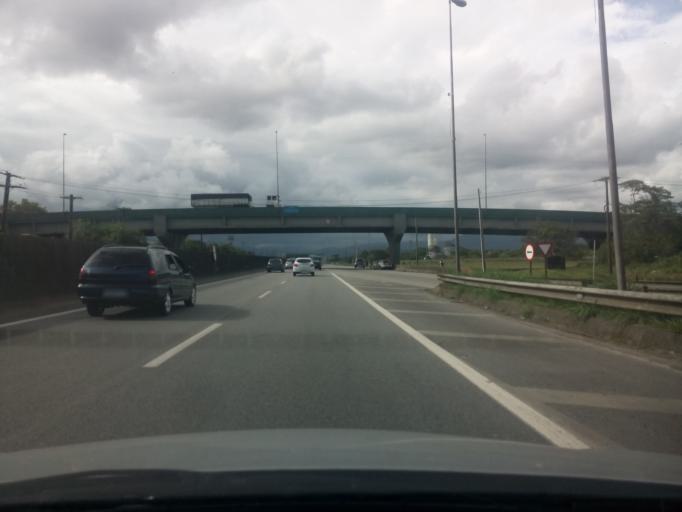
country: BR
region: Sao Paulo
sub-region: Guaruja
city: Guaruja
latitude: -23.9703
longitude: -46.2700
